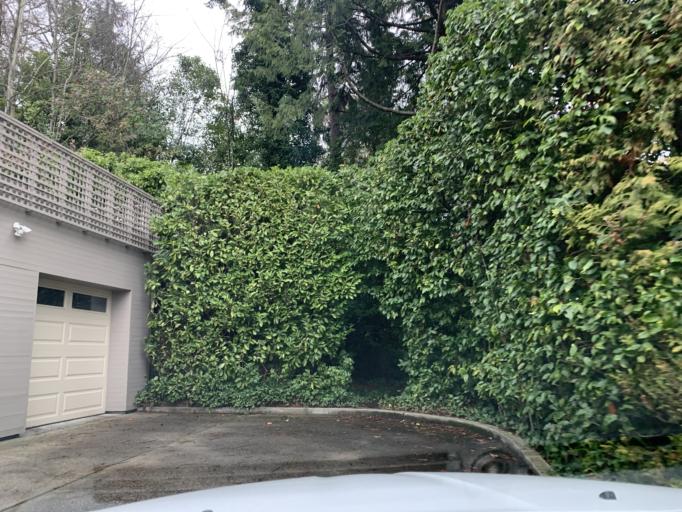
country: US
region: Washington
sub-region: King County
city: Medina
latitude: 47.6544
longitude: -122.2758
